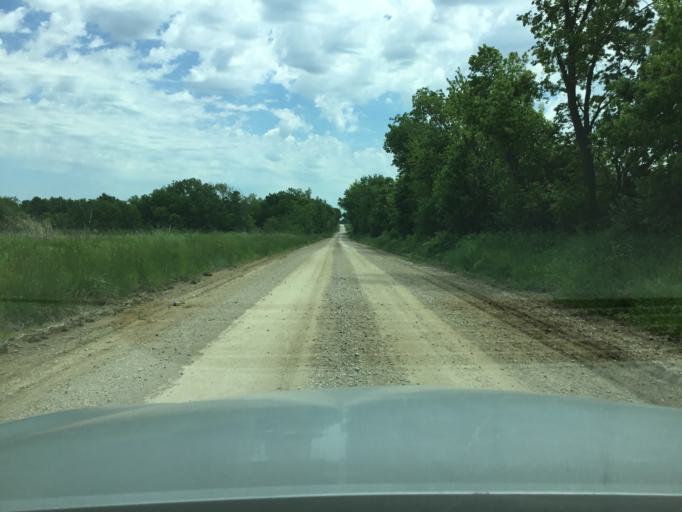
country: US
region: Kansas
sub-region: Montgomery County
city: Independence
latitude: 37.0952
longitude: -95.7957
